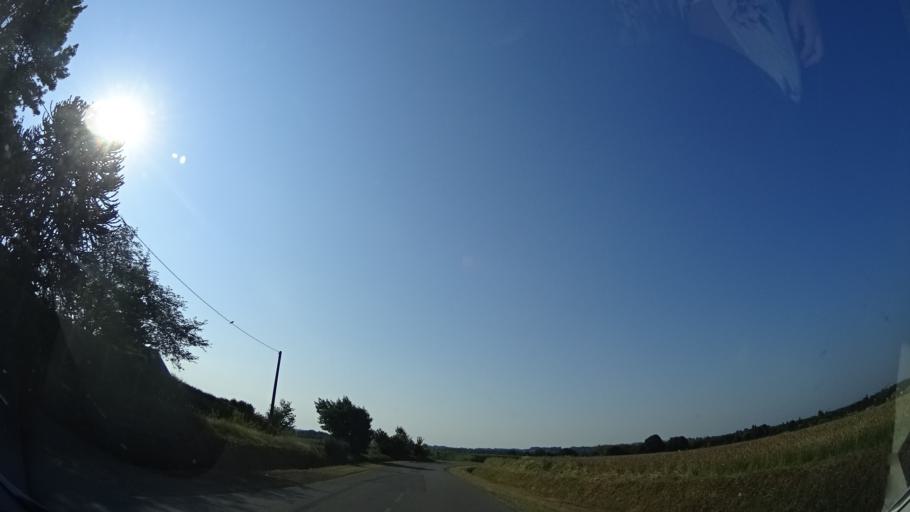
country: FR
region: Brittany
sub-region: Departement d'Ille-et-Vilaine
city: Pace
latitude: 48.1675
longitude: -1.7871
